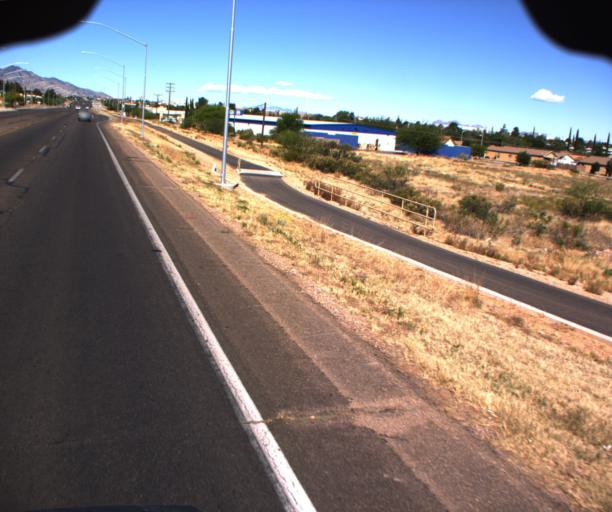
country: US
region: Arizona
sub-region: Cochise County
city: Sierra Vista
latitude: 31.5547
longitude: -110.2454
